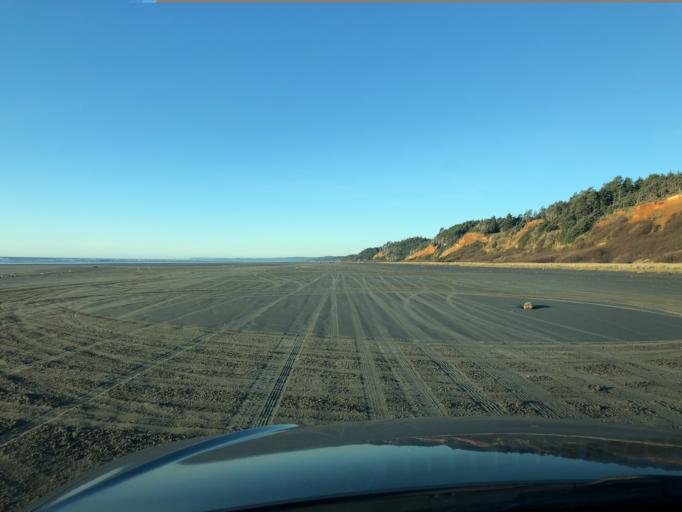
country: US
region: Washington
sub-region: Grays Harbor County
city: Ocean Shores
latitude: 47.1647
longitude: -124.1947
